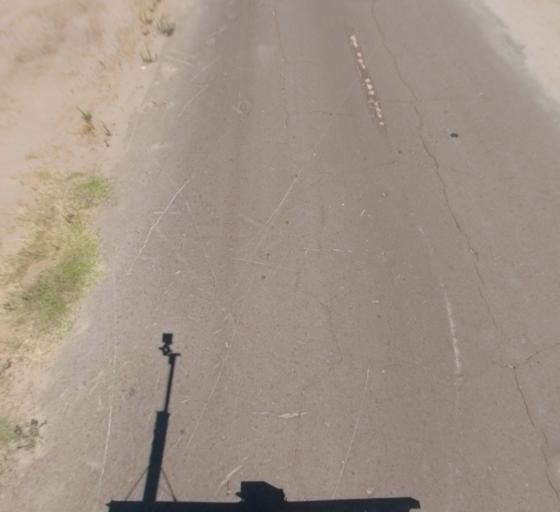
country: US
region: California
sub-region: Fresno County
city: Biola
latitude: 36.8539
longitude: -119.9831
